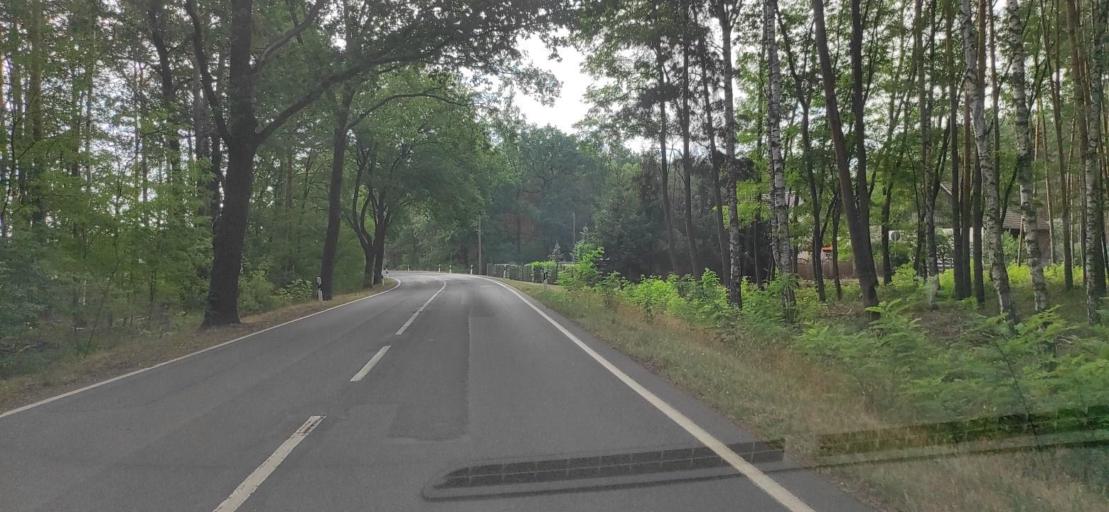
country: DE
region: Brandenburg
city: Forst
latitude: 51.7080
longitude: 14.6770
